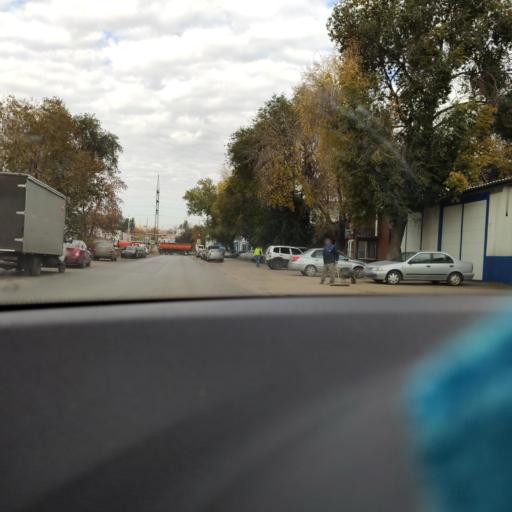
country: RU
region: Samara
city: Samara
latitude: 53.1979
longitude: 50.2579
